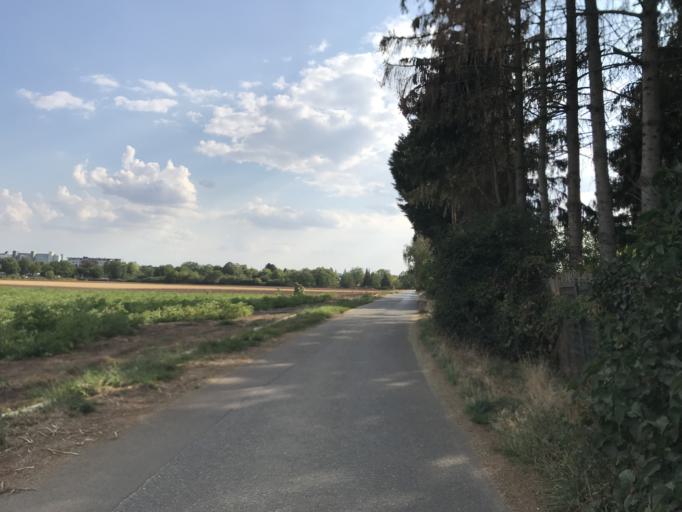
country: DE
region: Rheinland-Pfalz
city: Mainz
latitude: 50.0210
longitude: 8.2965
